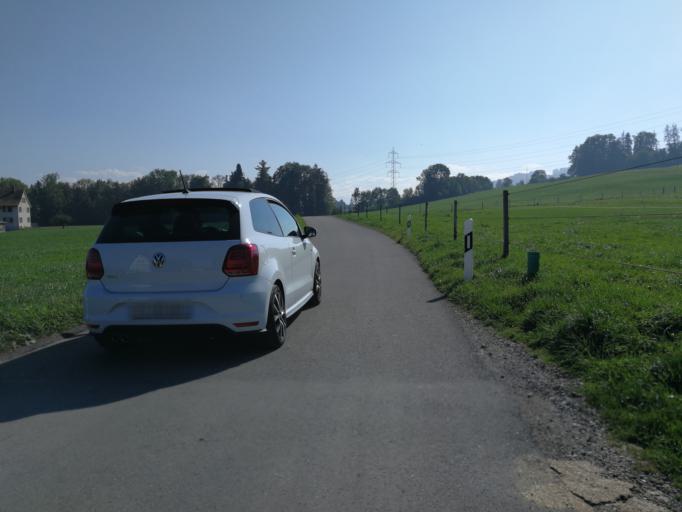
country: CH
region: Zurich
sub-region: Bezirk Uster
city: Hinteregg
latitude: 47.3164
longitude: 8.6844
